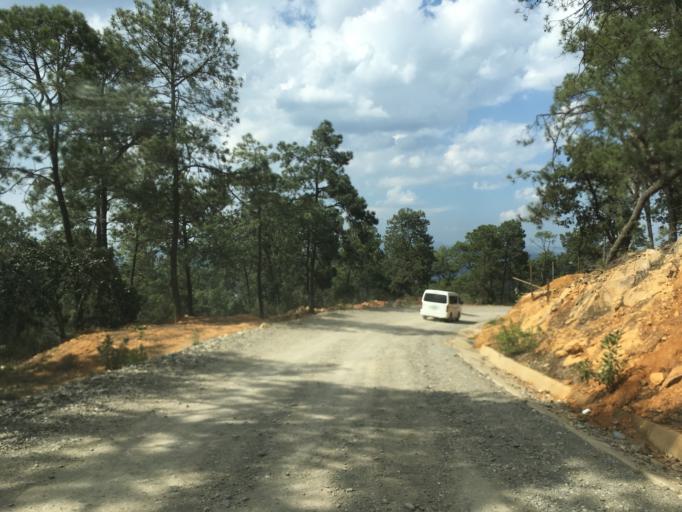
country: MX
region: Oaxaca
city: Santiago Tilantongo
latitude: 17.2078
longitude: -97.2783
